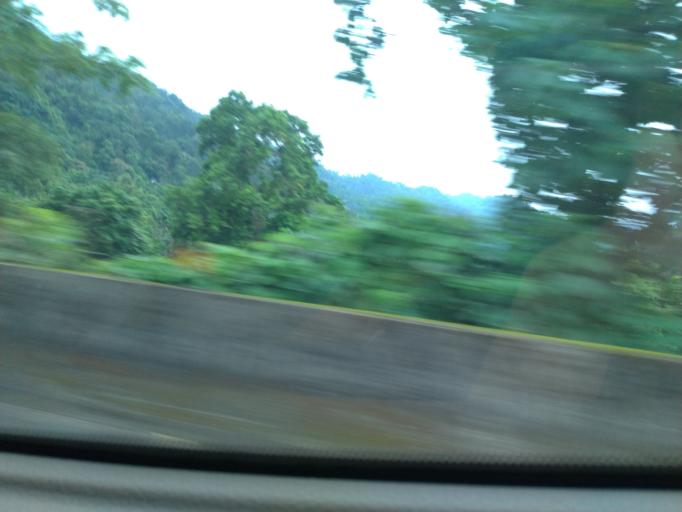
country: TW
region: Taipei
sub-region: Taipei
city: Banqiao
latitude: 24.9296
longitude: 121.4221
